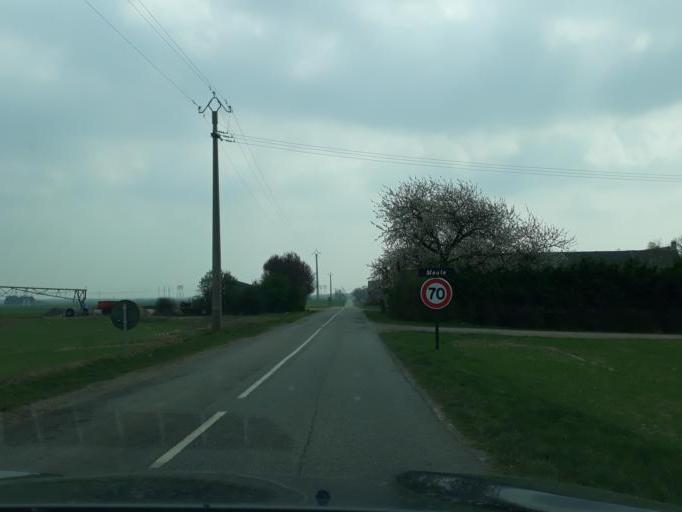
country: FR
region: Centre
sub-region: Departement du Loiret
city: Bricy
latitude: 48.0113
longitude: 1.8069
